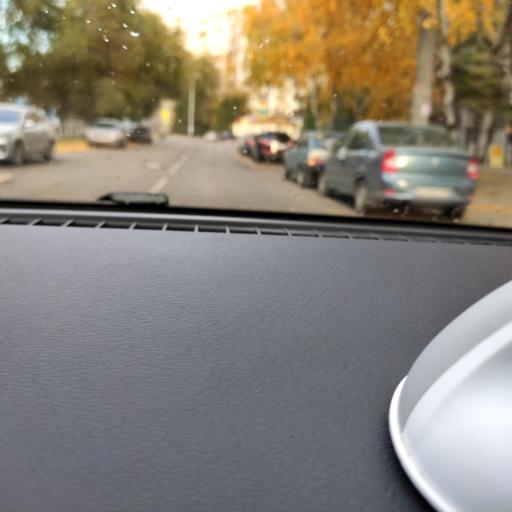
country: RU
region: Samara
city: Petra-Dubrava
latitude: 53.2342
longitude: 50.2715
